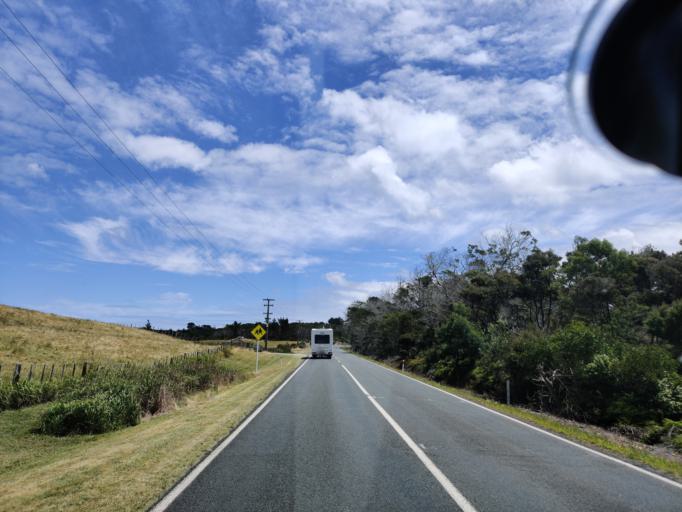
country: NZ
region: Northland
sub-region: Far North District
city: Kaitaia
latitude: -34.7847
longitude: 173.0984
